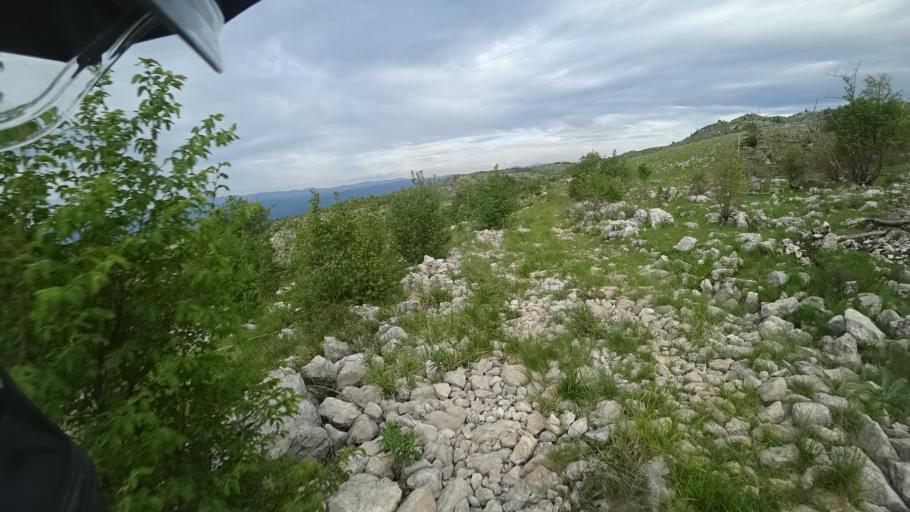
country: HR
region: Sibensko-Kniniska
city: Drnis
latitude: 43.8597
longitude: 16.3879
